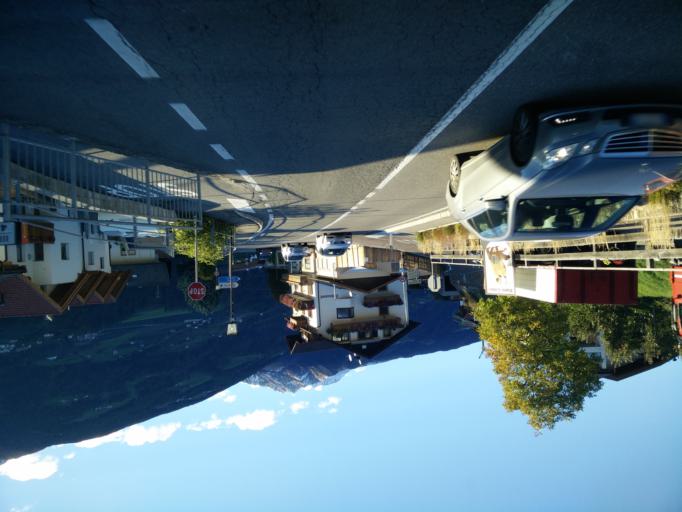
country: IT
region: Trentino-Alto Adige
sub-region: Bolzano
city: Caines
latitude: 46.6954
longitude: 11.1739
